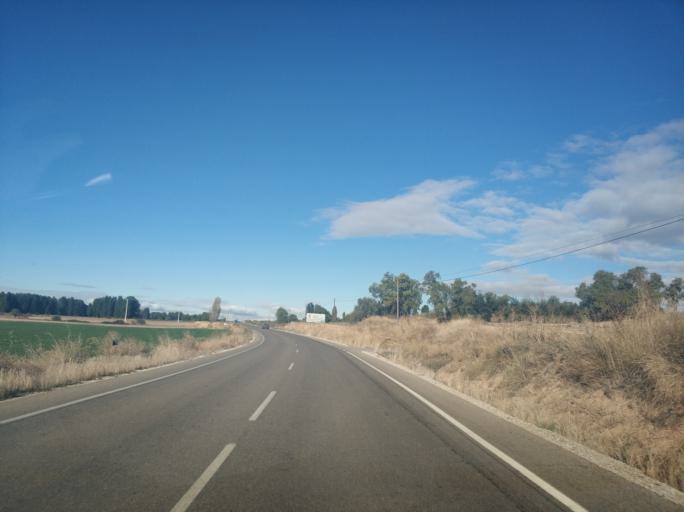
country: ES
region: Castille and Leon
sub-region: Provincia de Burgos
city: Penaranda de Duero
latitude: 41.6859
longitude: -3.4965
